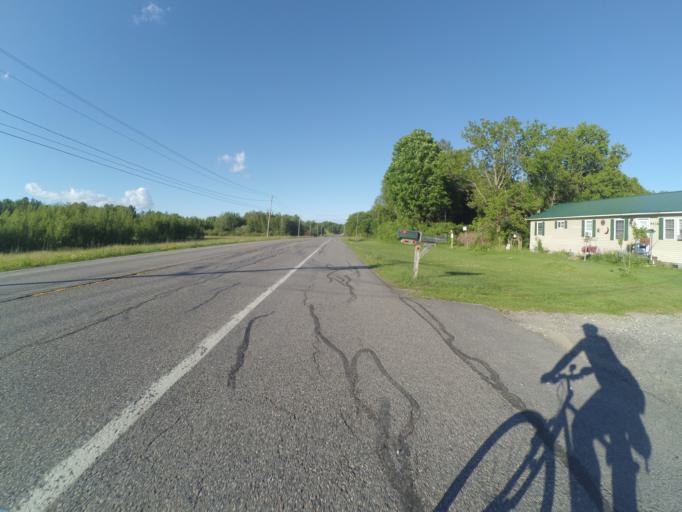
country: US
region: New York
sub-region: St. Lawrence County
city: Norwood
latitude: 44.7551
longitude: -74.8430
